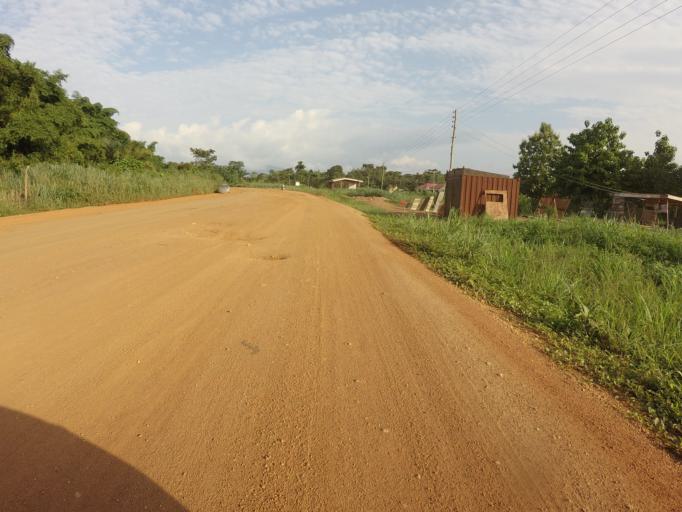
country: GH
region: Volta
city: Kpandu
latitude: 6.9914
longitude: 0.4399
